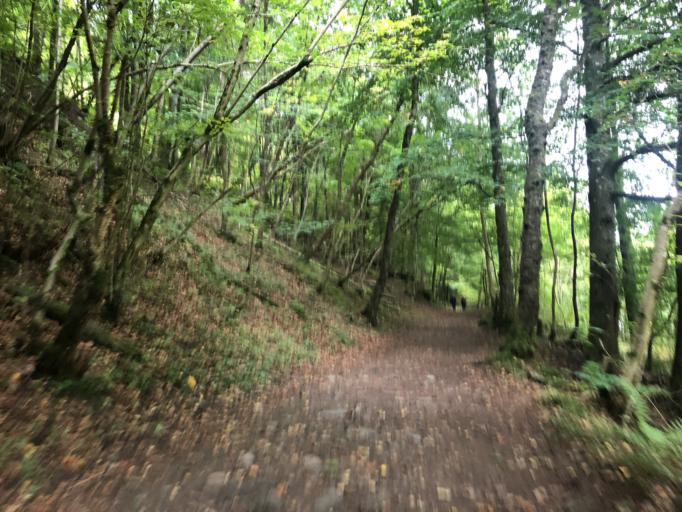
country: GB
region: Scotland
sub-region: Perth and Kinross
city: Pitlochry
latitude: 56.7375
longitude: -3.7722
